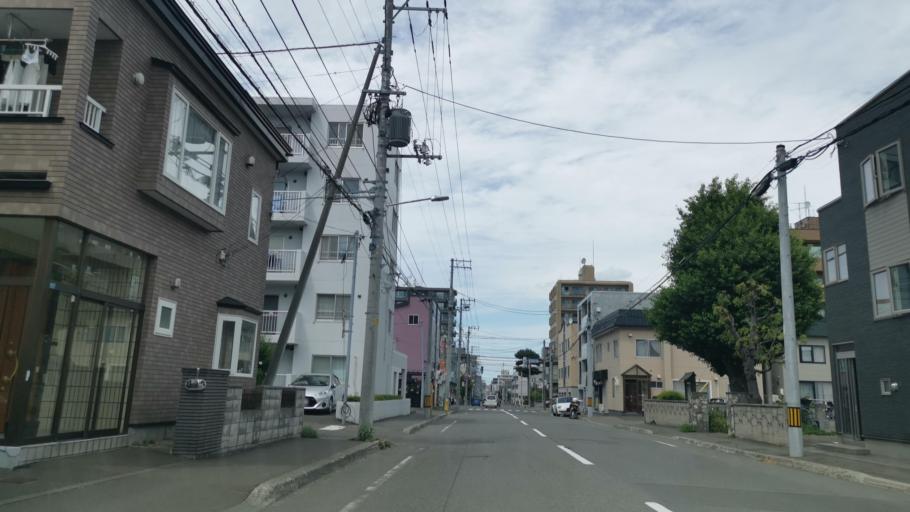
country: JP
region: Hokkaido
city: Sapporo
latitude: 43.0301
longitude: 141.3485
